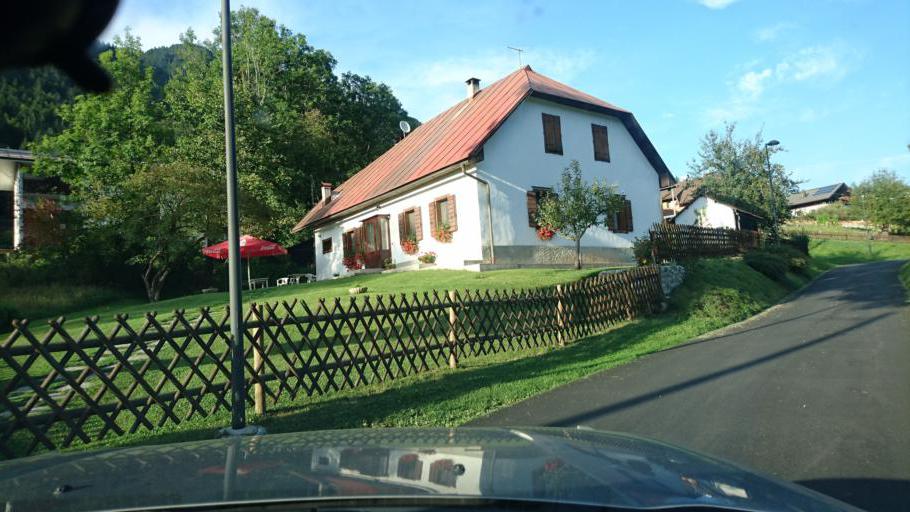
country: AT
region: Carinthia
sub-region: Politischer Bezirk Villach Land
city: Hohenthurn
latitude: 46.4963
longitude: 13.6526
